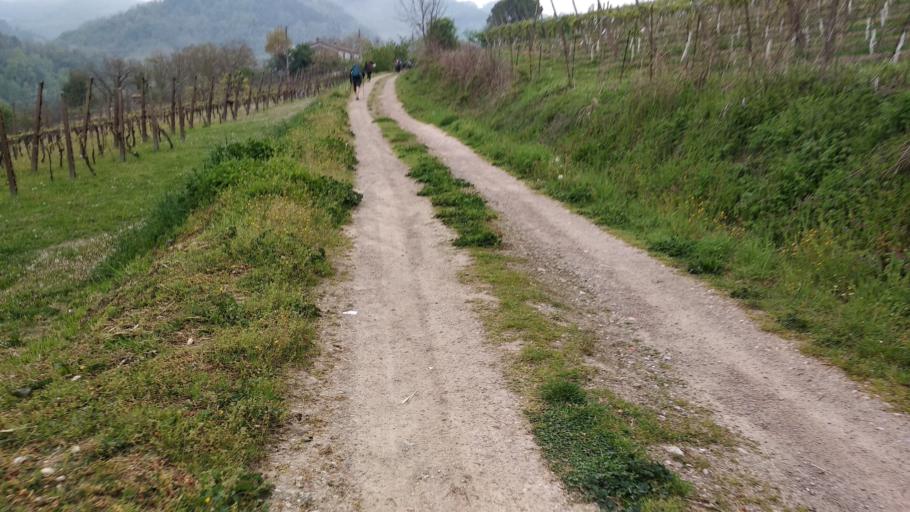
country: IT
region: Emilia-Romagna
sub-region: Forli-Cesena
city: Modigliana
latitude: 44.1468
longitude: 11.7983
